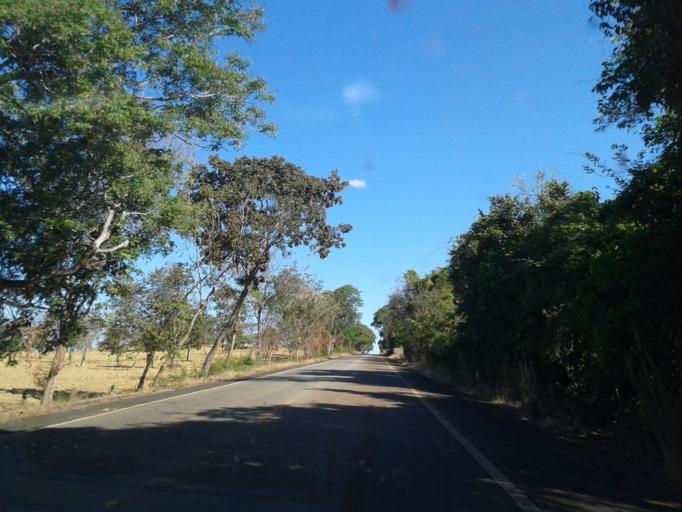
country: BR
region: Goias
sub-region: Mozarlandia
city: Mozarlandia
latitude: -14.6321
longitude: -50.5192
